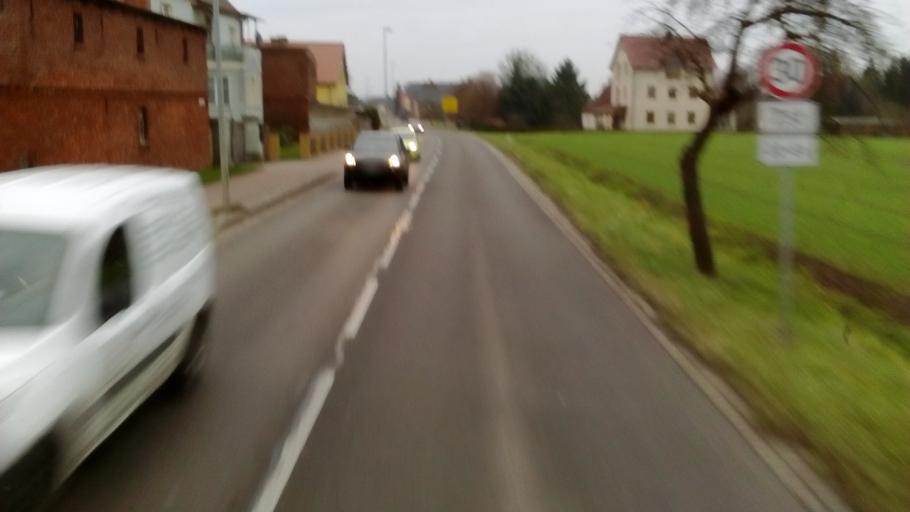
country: DE
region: Mecklenburg-Vorpommern
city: Viereck
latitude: 53.4946
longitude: 14.0862
